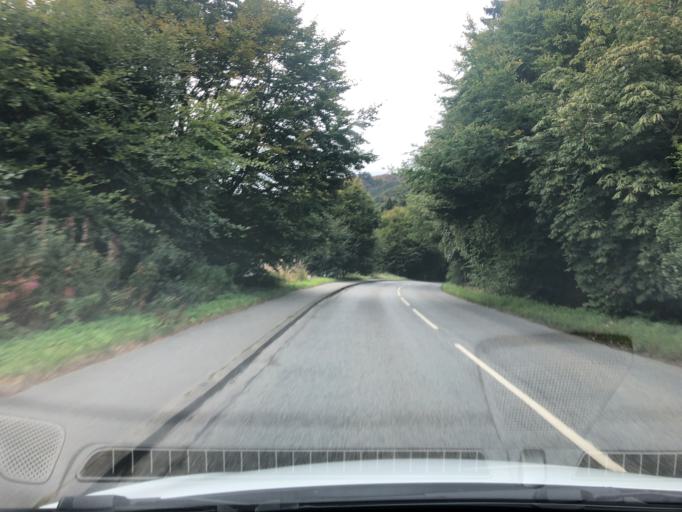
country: GB
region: Scotland
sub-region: Perth and Kinross
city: Pitlochry
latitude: 56.7224
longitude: -3.7720
